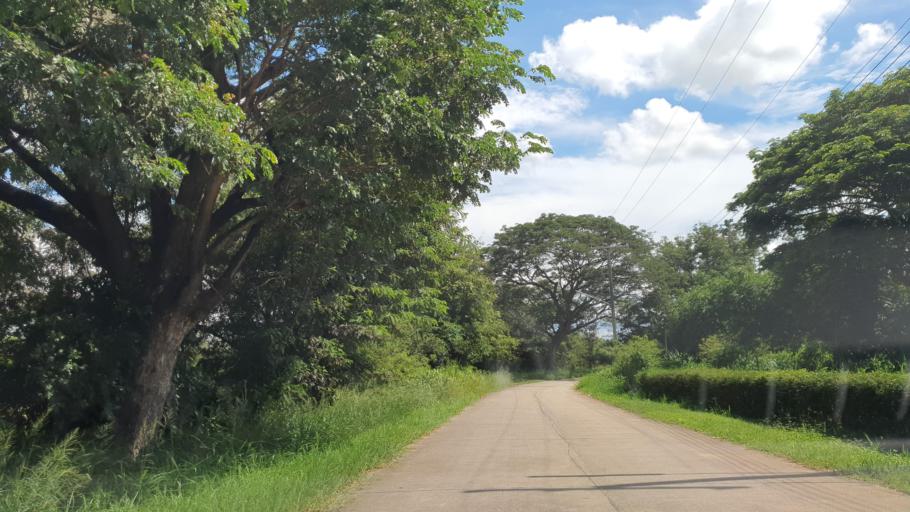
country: TH
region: Chiang Mai
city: San Pa Tong
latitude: 18.5779
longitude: 98.8743
